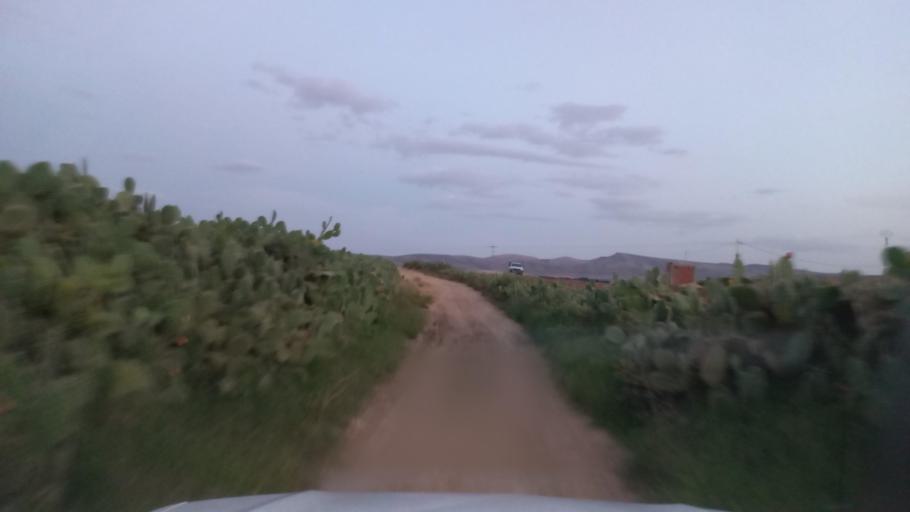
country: TN
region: Al Qasrayn
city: Sbiba
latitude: 35.4210
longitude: 9.1131
